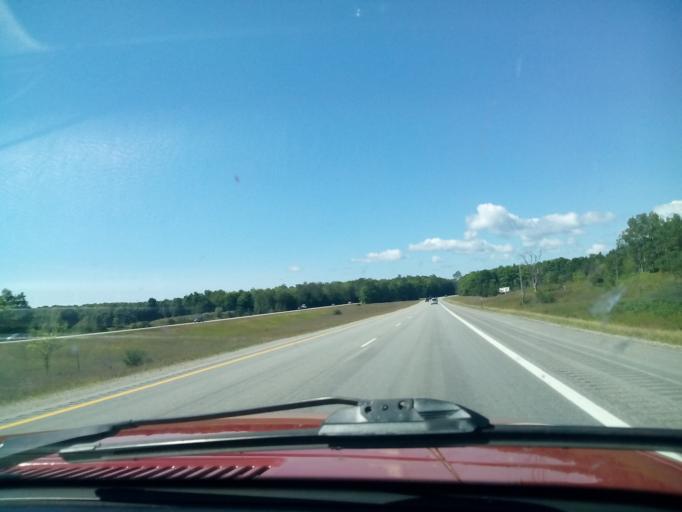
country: US
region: Michigan
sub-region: Cheboygan County
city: Indian River
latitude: 45.3198
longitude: -84.5980
